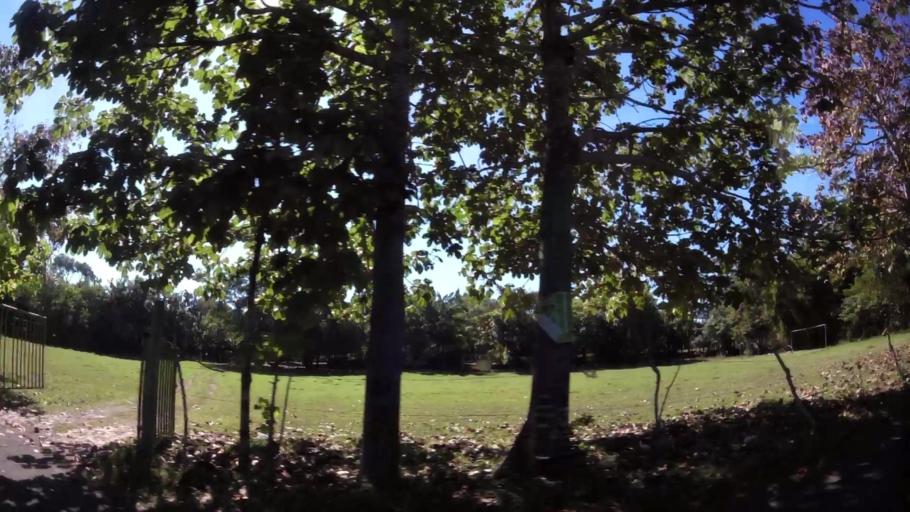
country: GT
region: Escuintla
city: Iztapa
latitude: 13.9232
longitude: -90.5969
